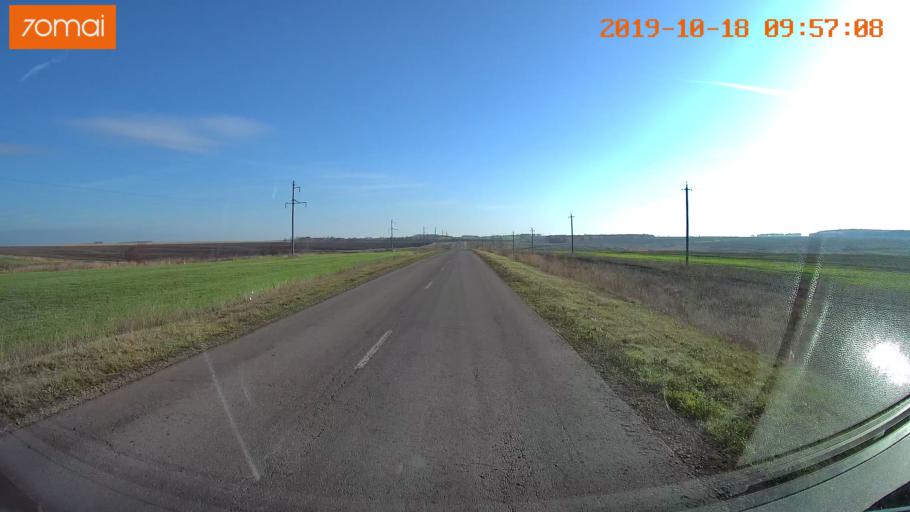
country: RU
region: Tula
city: Kurkino
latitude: 53.3763
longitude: 38.4083
